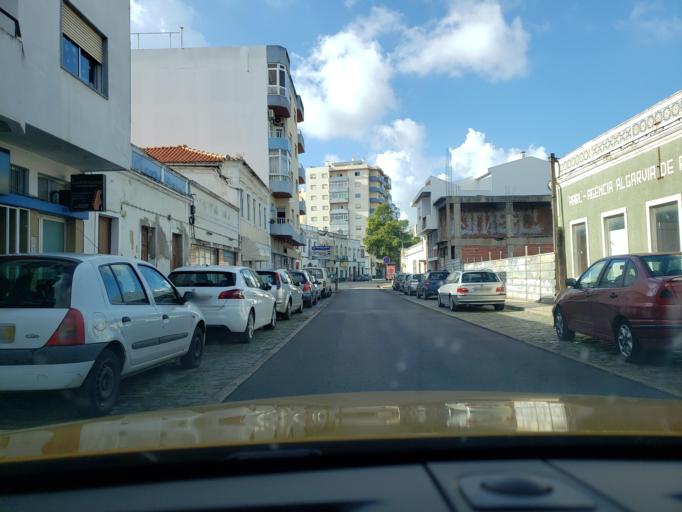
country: PT
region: Faro
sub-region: Portimao
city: Portimao
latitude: 37.1433
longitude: -8.5391
